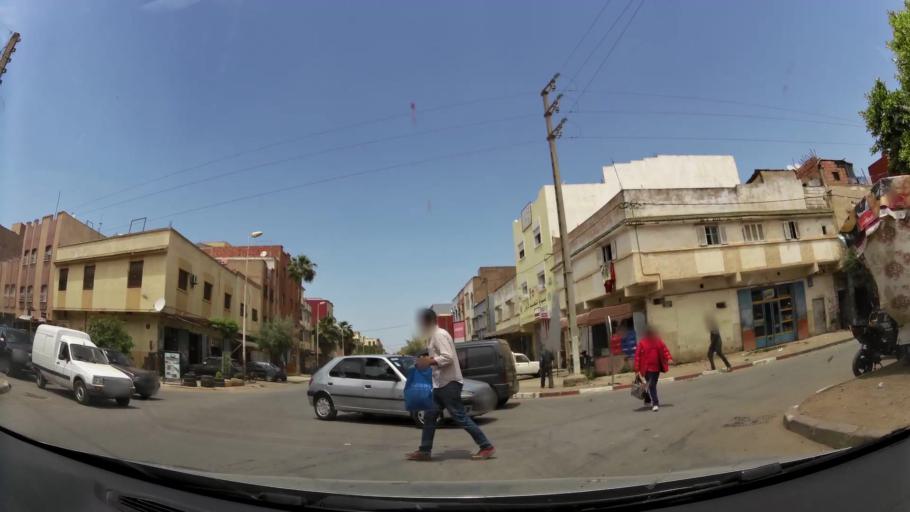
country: MA
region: Rabat-Sale-Zemmour-Zaer
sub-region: Khemisset
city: Khemisset
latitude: 33.8238
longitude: -6.0771
